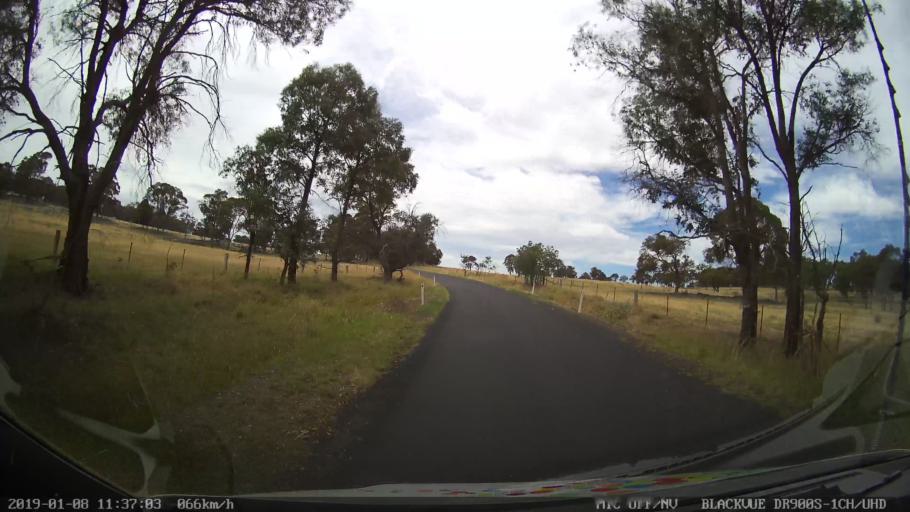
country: AU
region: New South Wales
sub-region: Guyra
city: Guyra
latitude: -30.3497
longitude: 151.5487
